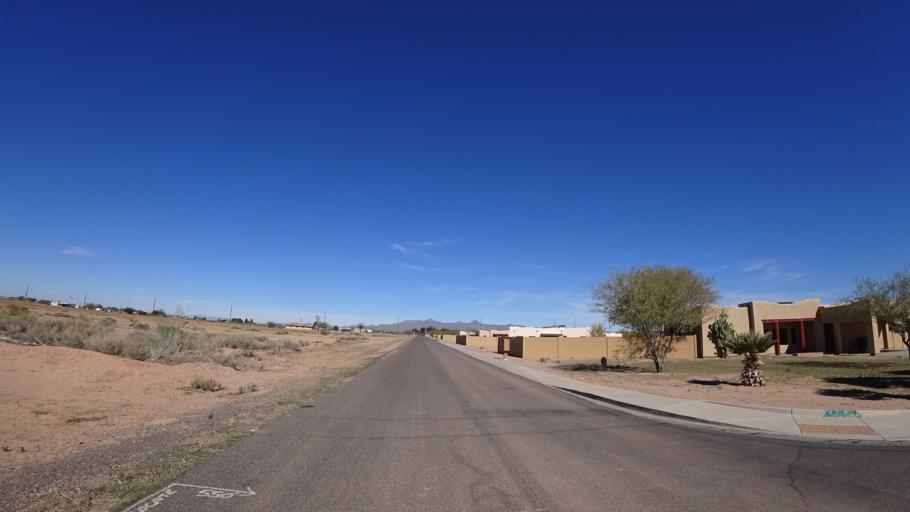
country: US
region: Arizona
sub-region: Maricopa County
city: Mesa
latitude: 33.4920
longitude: -111.8166
